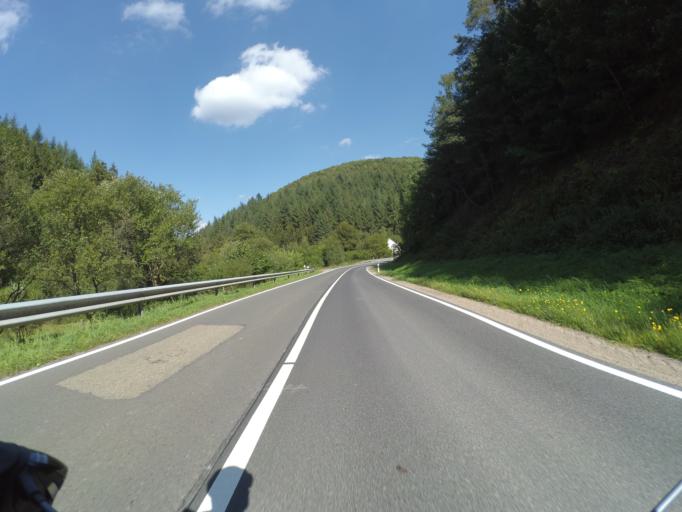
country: DE
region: Rheinland-Pfalz
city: Herl
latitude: 49.7330
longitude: 6.8310
